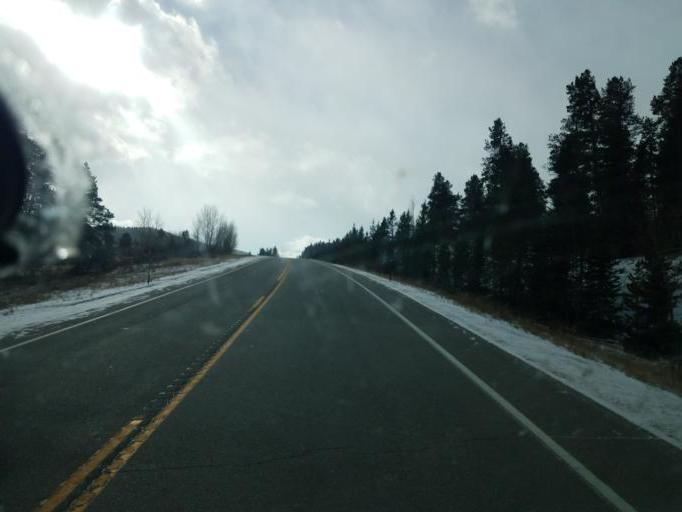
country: US
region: Colorado
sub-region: Summit County
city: Breckenridge
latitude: 39.4190
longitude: -105.7644
